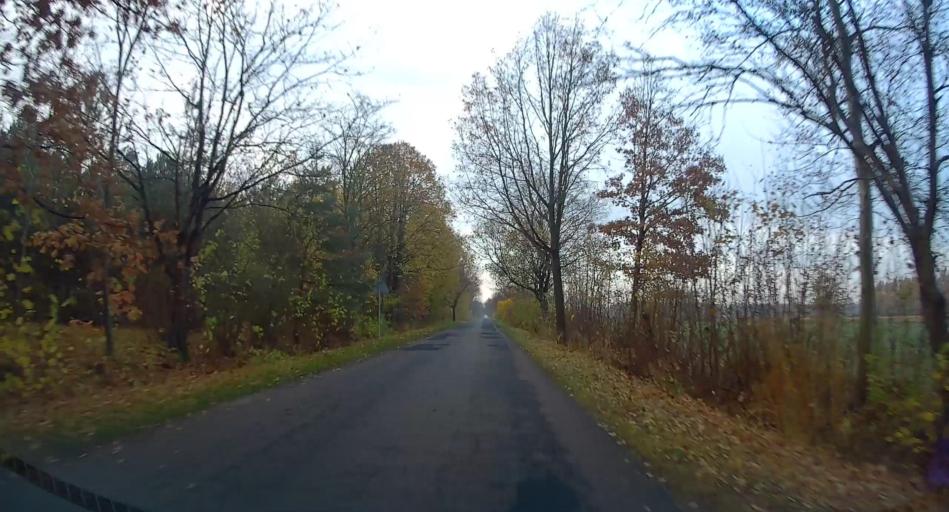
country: PL
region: Masovian Voivodeship
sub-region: Powiat zyrardowski
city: Puszcza Marianska
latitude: 51.9386
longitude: 20.3673
